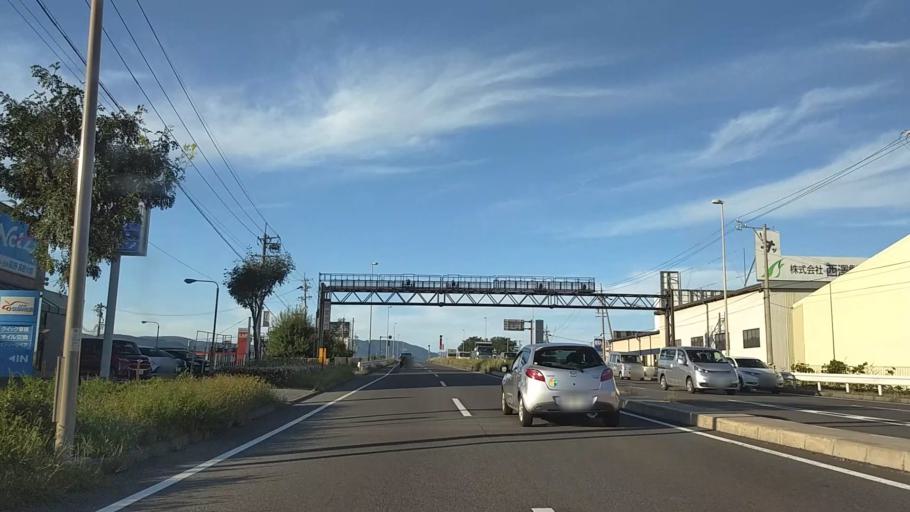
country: JP
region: Nagano
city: Nagano-shi
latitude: 36.6147
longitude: 138.1975
